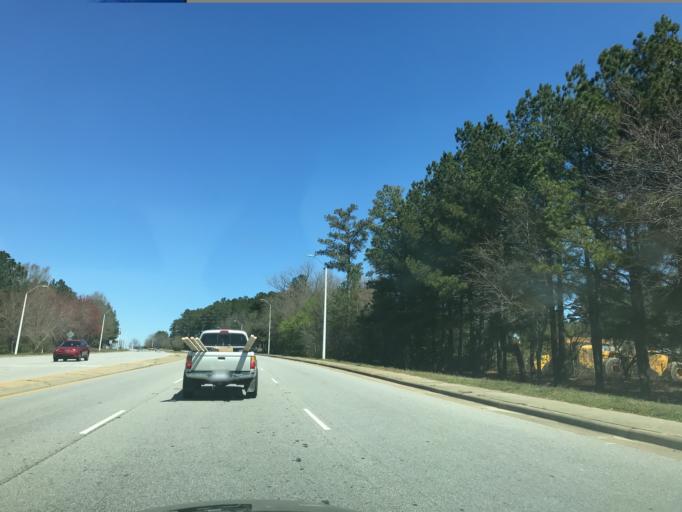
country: US
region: North Carolina
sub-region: Wake County
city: Garner
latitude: 35.7202
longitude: -78.6382
